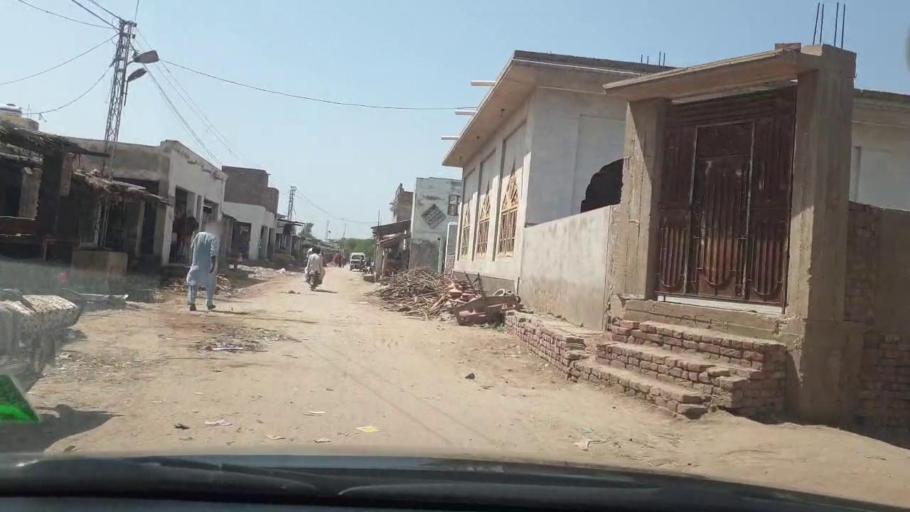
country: PK
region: Sindh
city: Tando Bago
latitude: 24.9263
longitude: 69.0567
